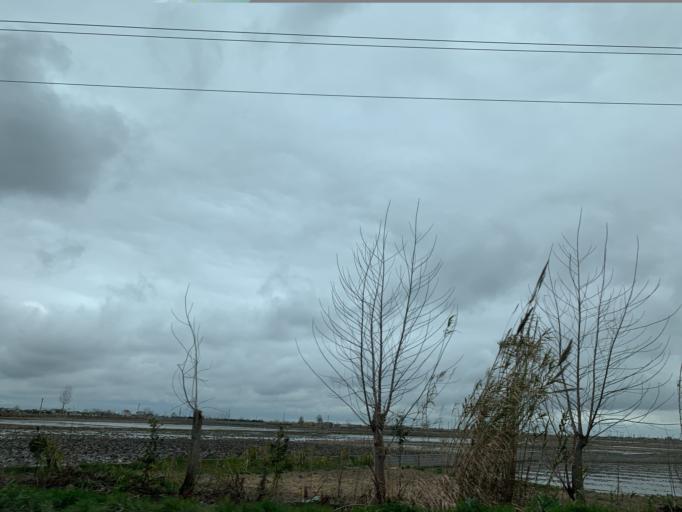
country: IR
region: Mazandaran
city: Babol
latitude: 36.5069
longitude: 52.5410
